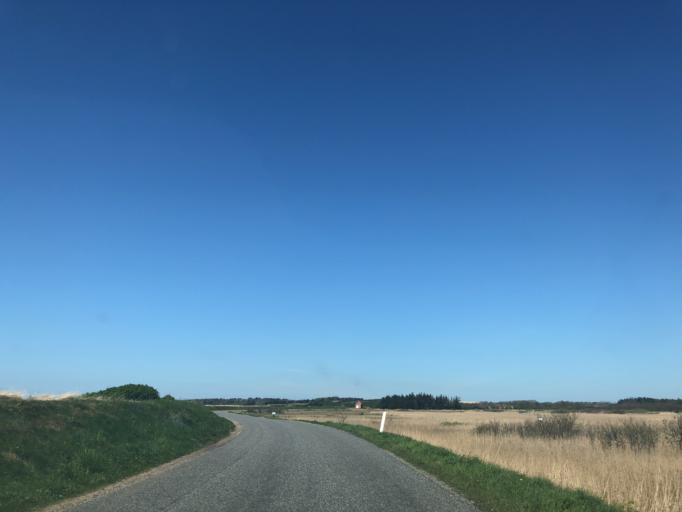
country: DK
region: Central Jutland
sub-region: Holstebro Kommune
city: Vinderup
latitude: 56.5517
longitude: 8.7673
